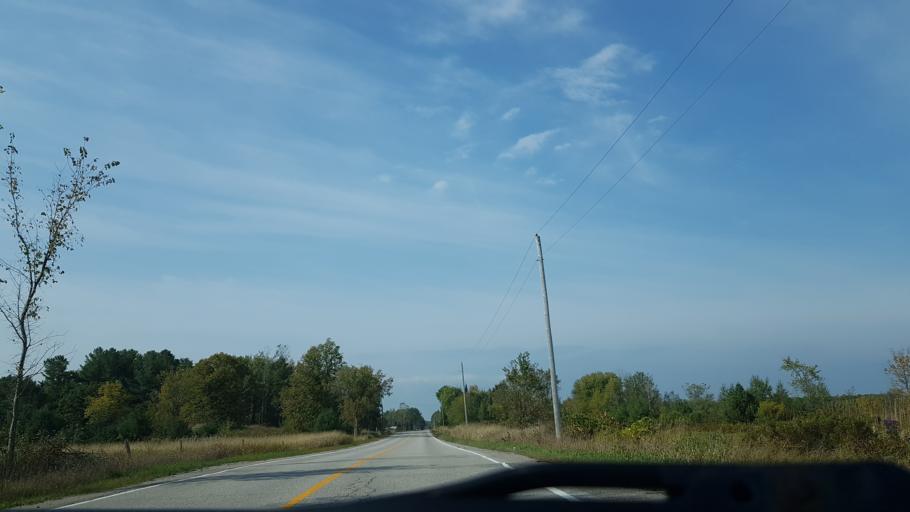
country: CA
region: Ontario
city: Gravenhurst
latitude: 44.7786
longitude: -79.2797
